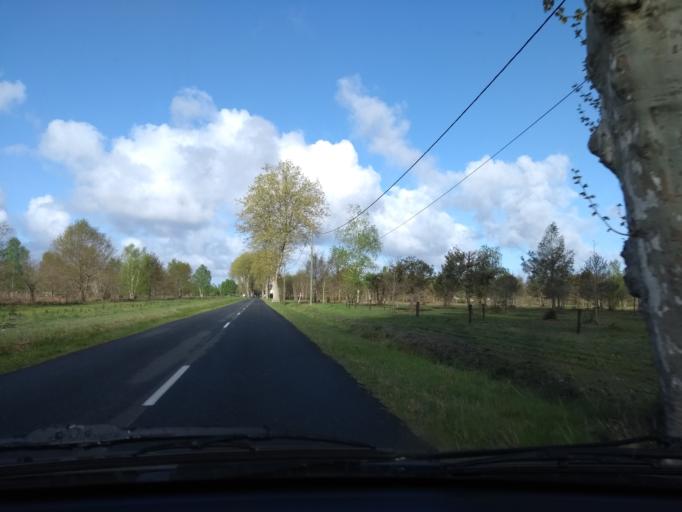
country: FR
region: Aquitaine
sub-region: Departement de la Gironde
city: Mios
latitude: 44.5497
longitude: -0.9853
